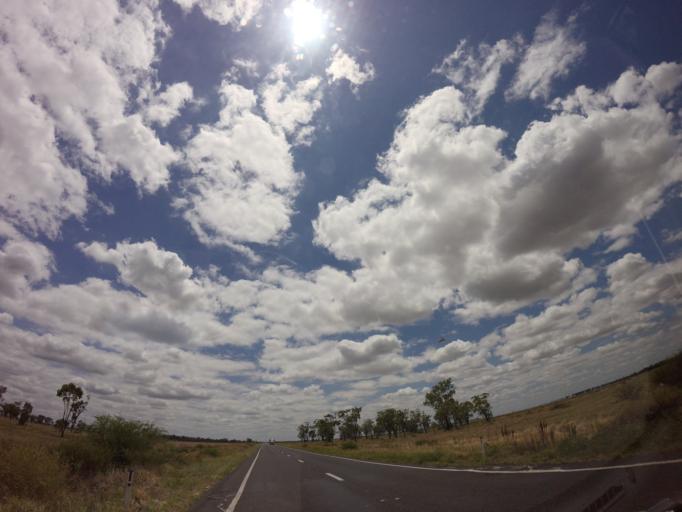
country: AU
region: New South Wales
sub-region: Moree Plains
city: Boggabilla
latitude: -28.6833
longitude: 150.3021
